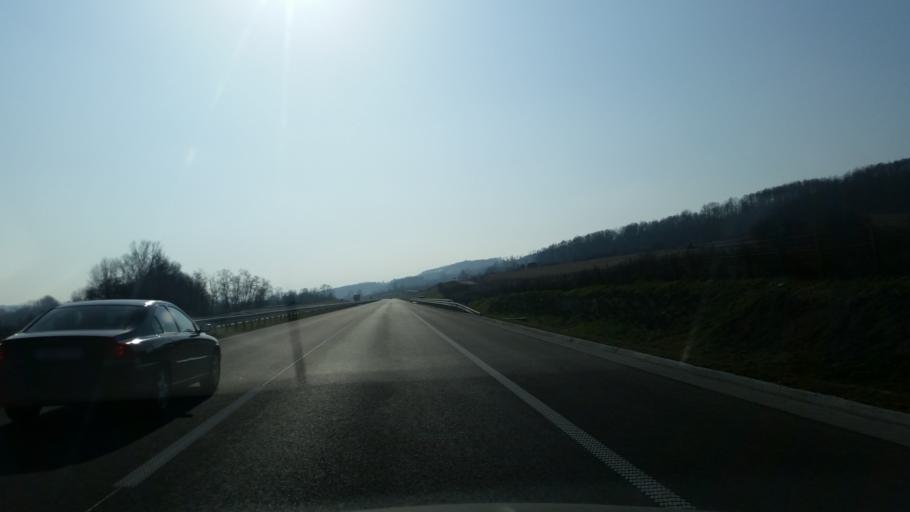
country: RS
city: Prislonica
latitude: 43.9497
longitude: 20.4007
